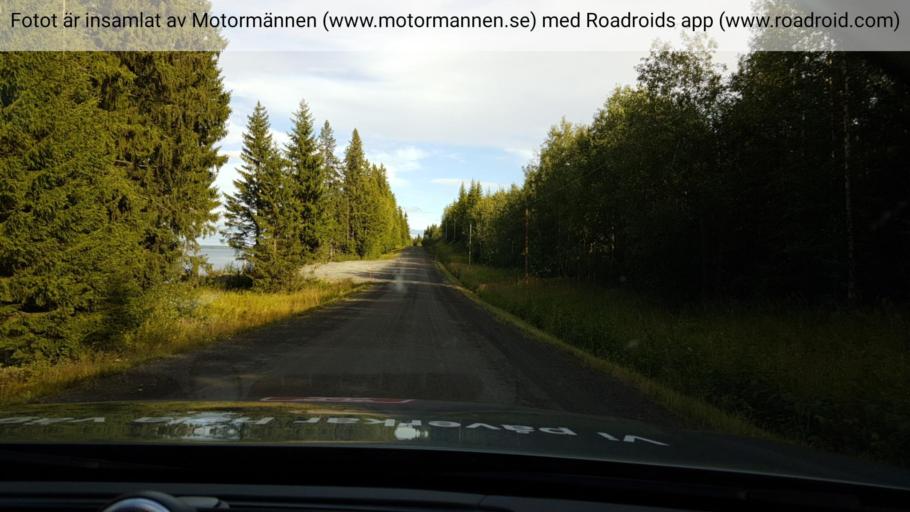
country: SE
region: Jaemtland
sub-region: Stroemsunds Kommun
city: Stroemsund
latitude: 64.1396
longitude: 15.7434
